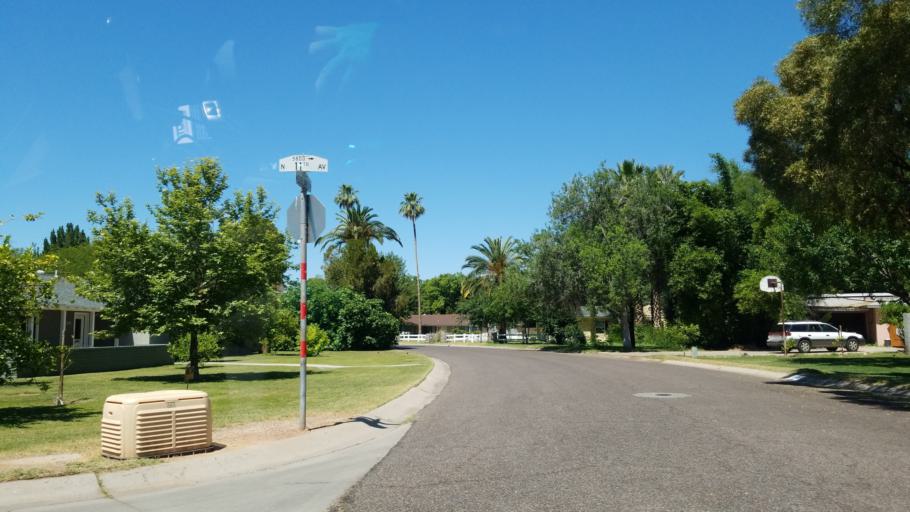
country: US
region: Arizona
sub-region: Maricopa County
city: Phoenix
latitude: 33.5216
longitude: -112.0868
